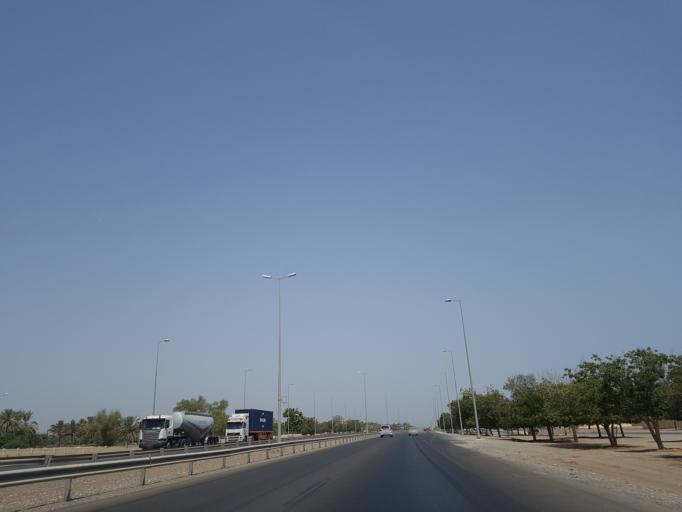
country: OM
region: Al Batinah
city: Saham
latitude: 24.0916
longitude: 56.9282
